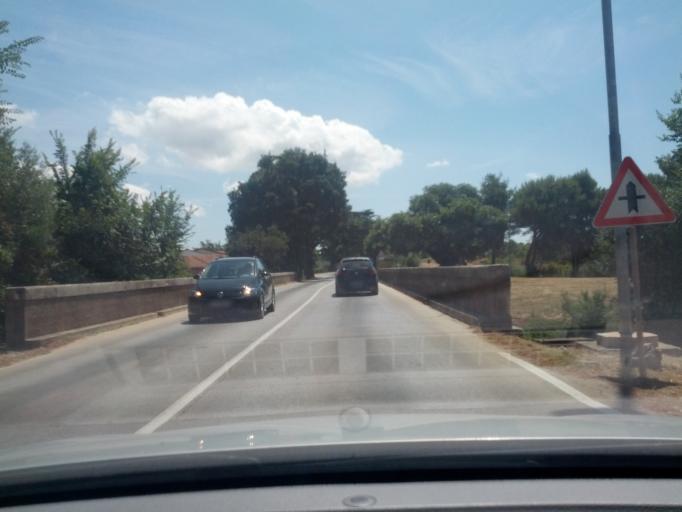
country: HR
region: Istarska
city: Fazana
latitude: 44.9153
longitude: 13.8156
